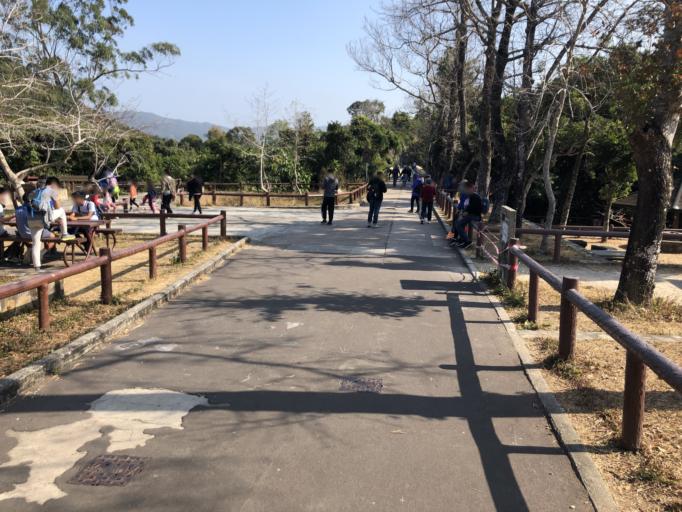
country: HK
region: Wanchai
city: Wan Chai
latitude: 22.2492
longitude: 114.2133
